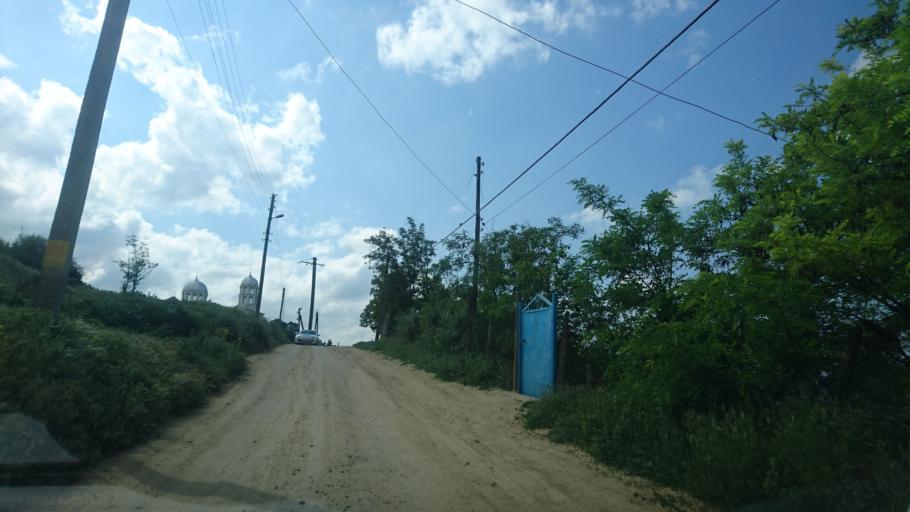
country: MD
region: Telenesti
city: Cocieri
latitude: 47.3581
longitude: 29.1057
